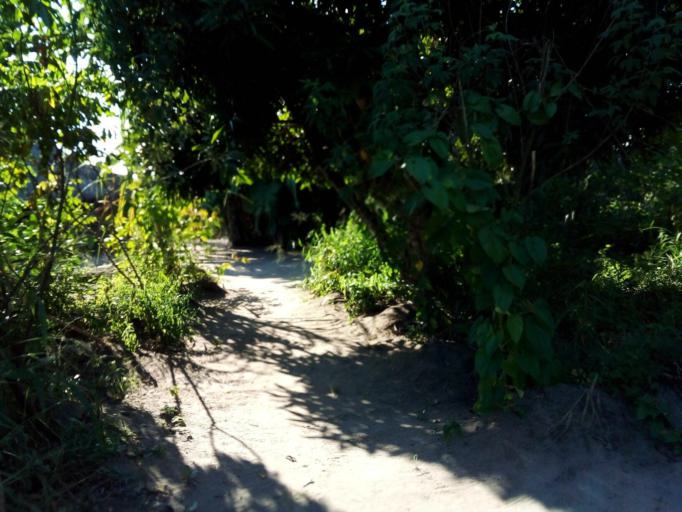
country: MZ
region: Zambezia
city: Quelimane
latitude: -17.5739
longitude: 36.8665
